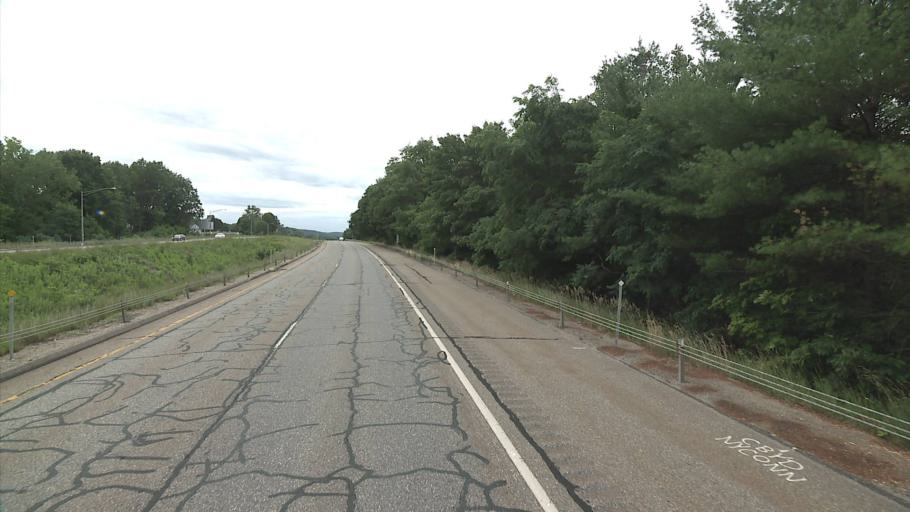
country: US
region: Connecticut
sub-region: Litchfield County
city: Torrington
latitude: 41.8158
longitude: -73.1138
